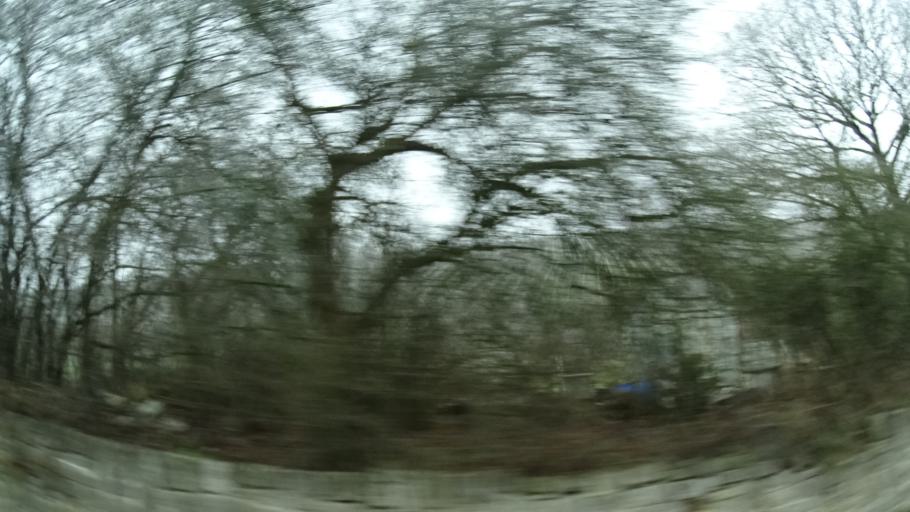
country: DE
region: Bavaria
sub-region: Regierungsbezirk Unterfranken
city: Frickenhausen
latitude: 49.6704
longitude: 10.1053
